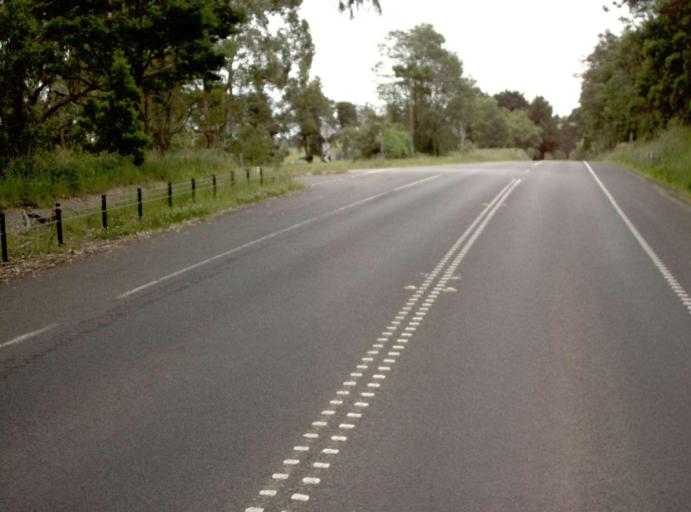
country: AU
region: Victoria
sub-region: Bass Coast
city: North Wonthaggi
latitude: -38.4211
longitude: 145.7911
